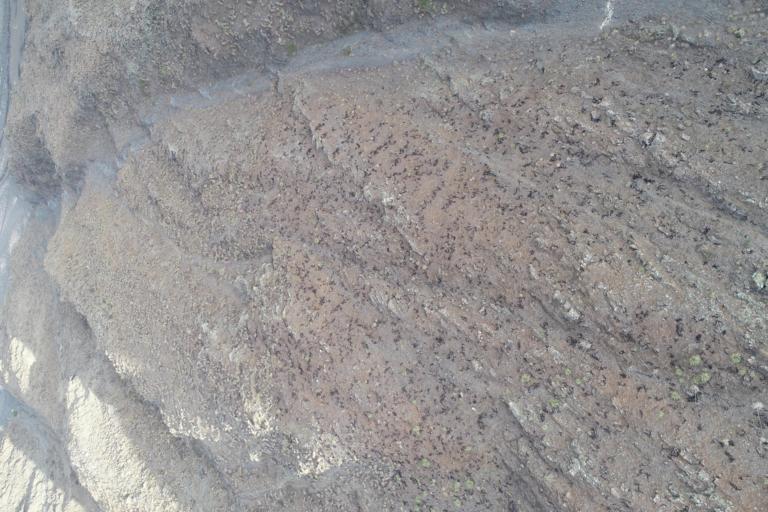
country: BO
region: La Paz
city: Sorata
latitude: -15.5209
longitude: -68.6904
